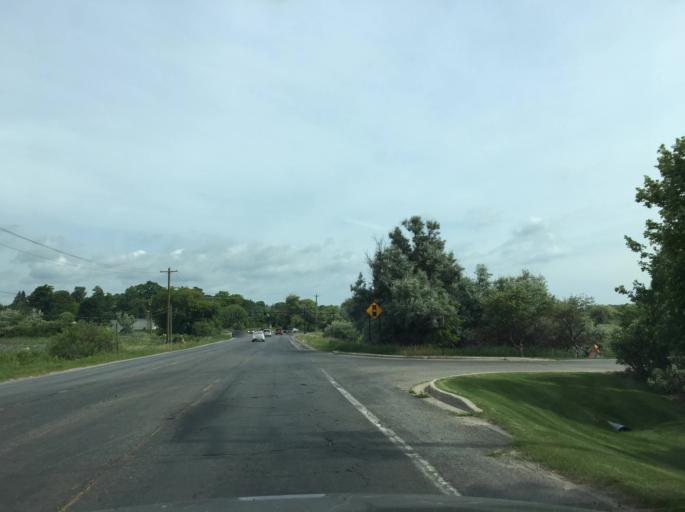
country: US
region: Michigan
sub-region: Grand Traverse County
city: Traverse City
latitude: 44.7458
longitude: -85.6454
